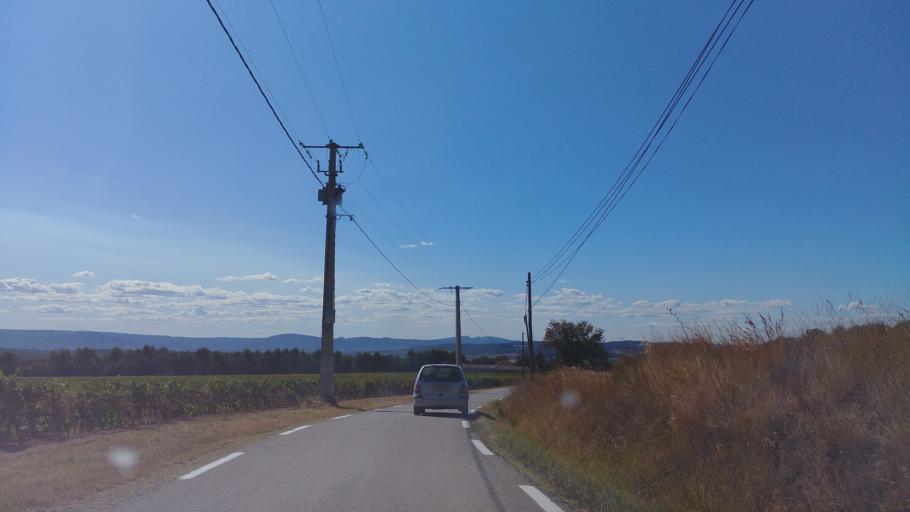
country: FR
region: Provence-Alpes-Cote d'Azur
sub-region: Departement du Vaucluse
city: Grambois
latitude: 43.7248
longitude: 5.5911
